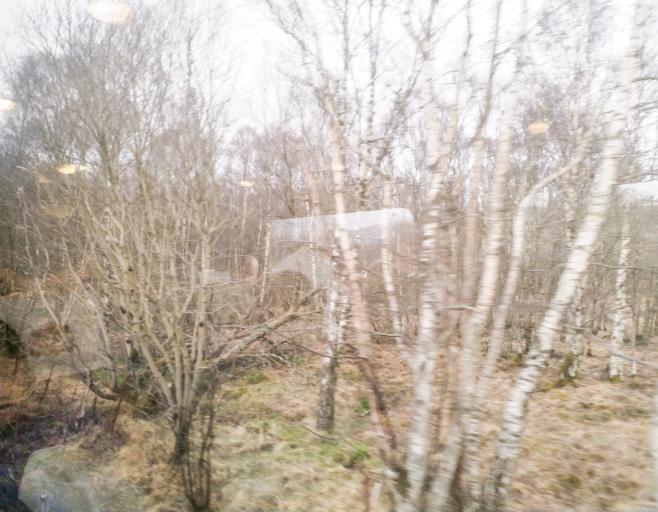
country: GB
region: Scotland
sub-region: Highland
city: Spean Bridge
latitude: 56.8878
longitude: -4.8329
